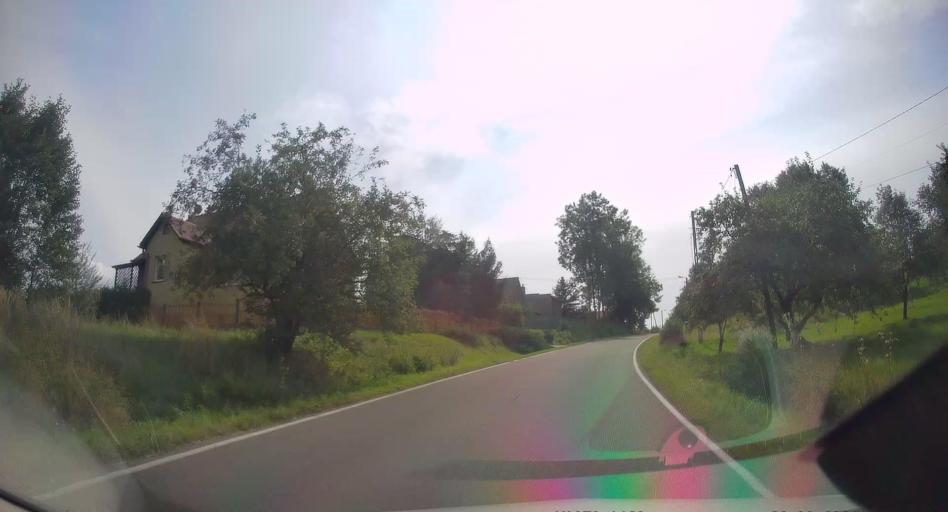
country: PL
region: Lesser Poland Voivodeship
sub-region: Powiat wielicki
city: Pawlikowice
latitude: 49.9494
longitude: 20.0422
